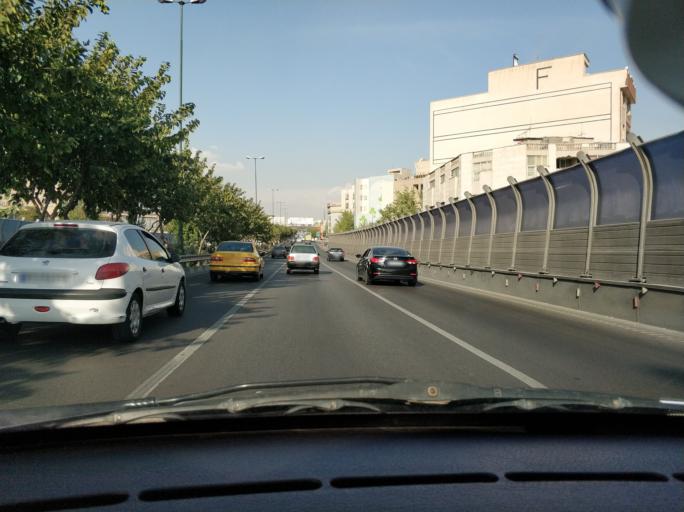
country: IR
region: Tehran
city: Tehran
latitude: 35.7213
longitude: 51.3609
